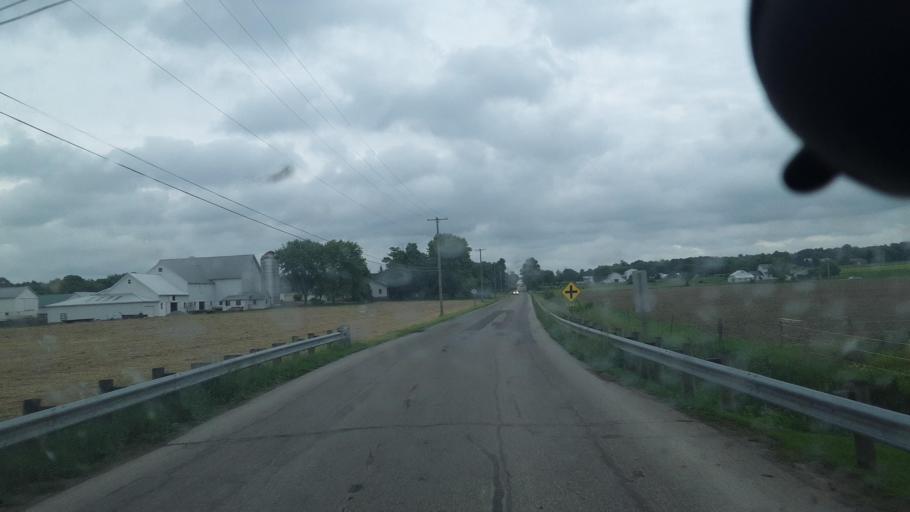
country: US
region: Ohio
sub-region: Geauga County
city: Middlefield
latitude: 41.4794
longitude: -81.0254
